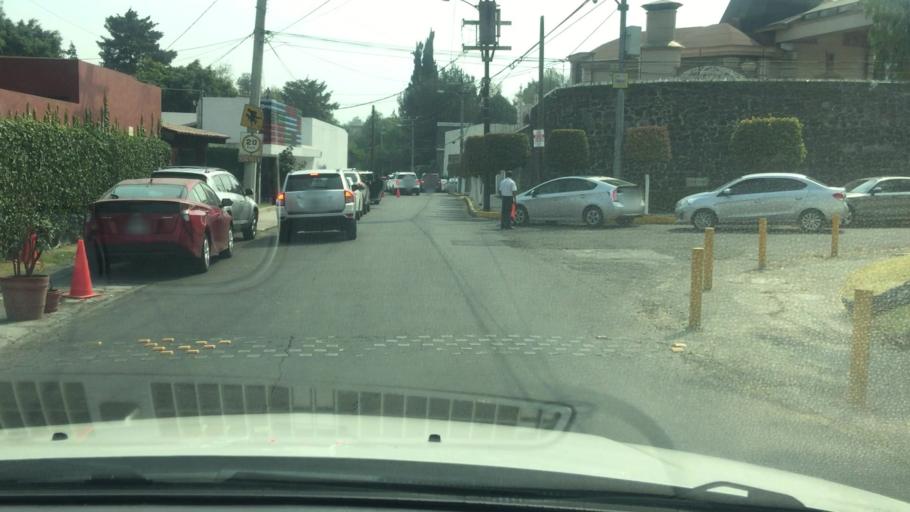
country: MX
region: Mexico City
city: Magdalena Contreras
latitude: 19.3146
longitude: -99.2091
